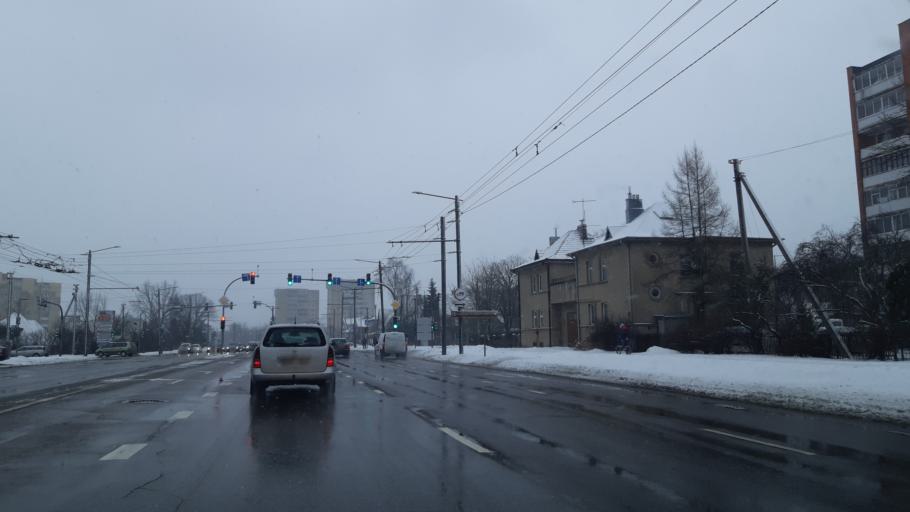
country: LT
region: Kauno apskritis
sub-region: Kaunas
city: Eiguliai
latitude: 54.9113
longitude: 23.9409
